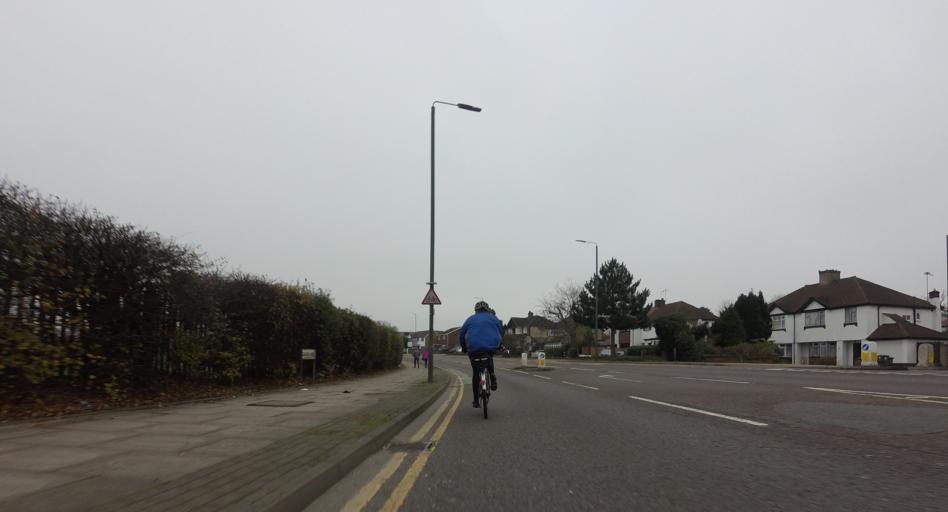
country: GB
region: England
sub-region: Greater London
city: Bexley
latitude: 51.4525
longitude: 0.1520
